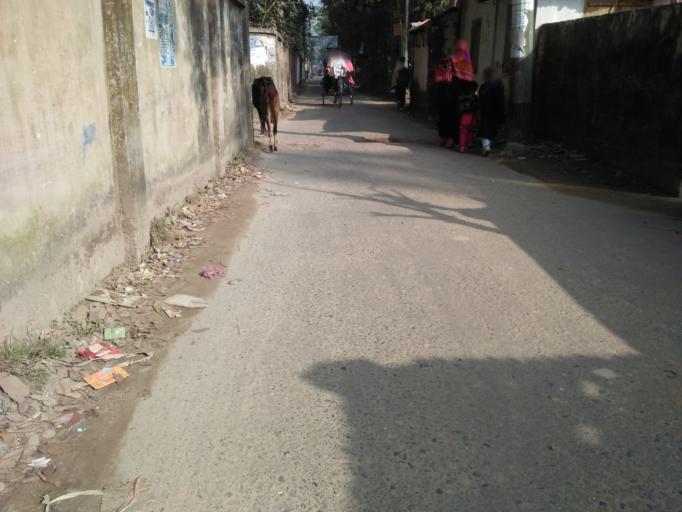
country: BD
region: Barisal
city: Bhola
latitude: 22.6799
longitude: 90.6425
